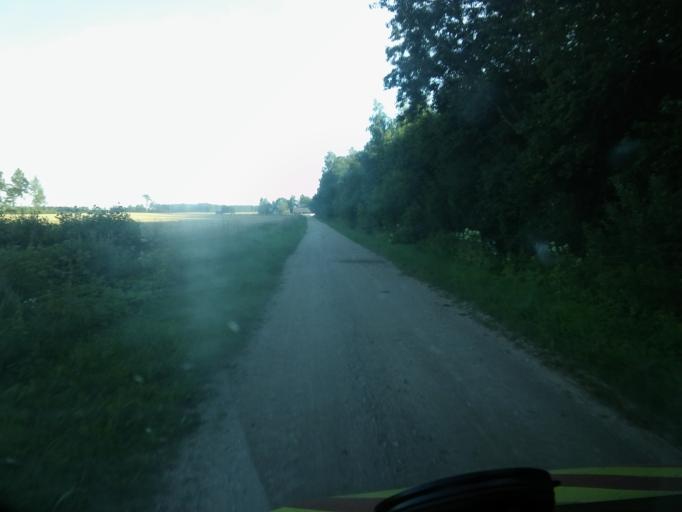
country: EE
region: Valgamaa
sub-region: Torva linn
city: Torva
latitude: 58.0910
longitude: 25.9945
